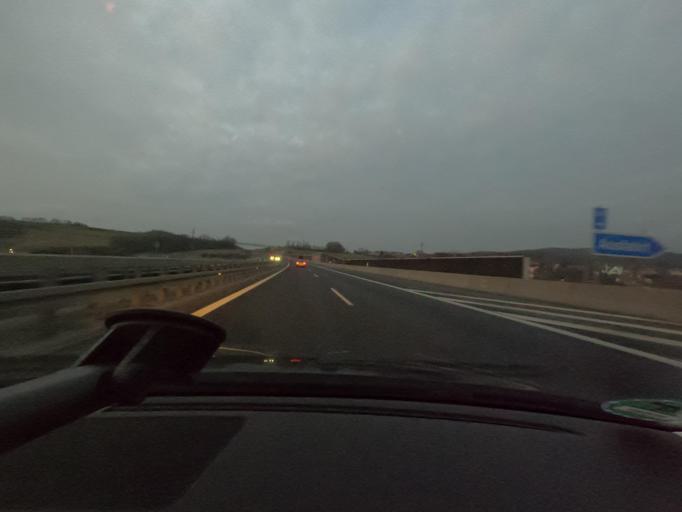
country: DE
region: Bavaria
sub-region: Upper Franconia
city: Lichtenfels
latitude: 50.1453
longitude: 11.0323
